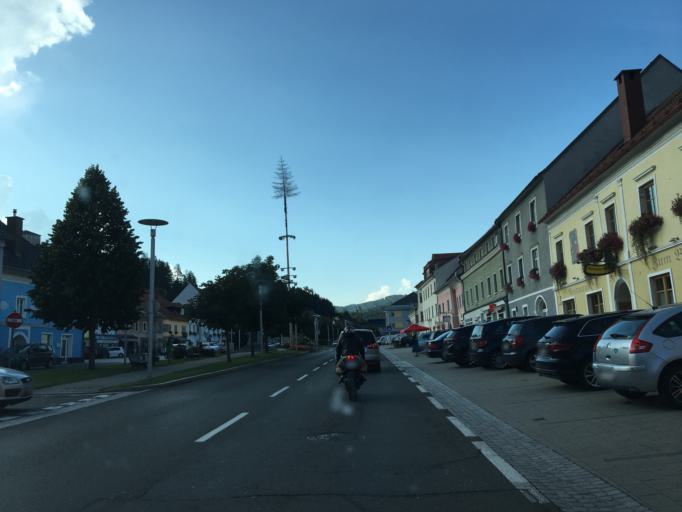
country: AT
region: Styria
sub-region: Politischer Bezirk Murau
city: Neumarkt in Steiermark
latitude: 47.0716
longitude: 14.4271
